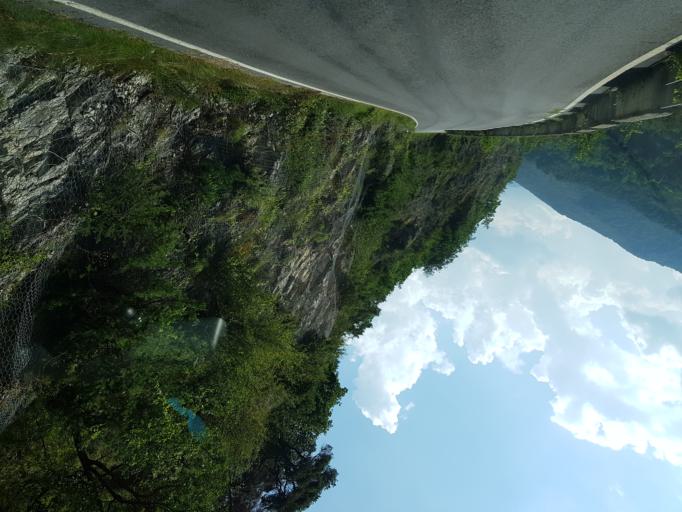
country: IT
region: Piedmont
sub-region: Provincia di Cuneo
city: San Damiano Macra
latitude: 44.4908
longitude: 7.2233
